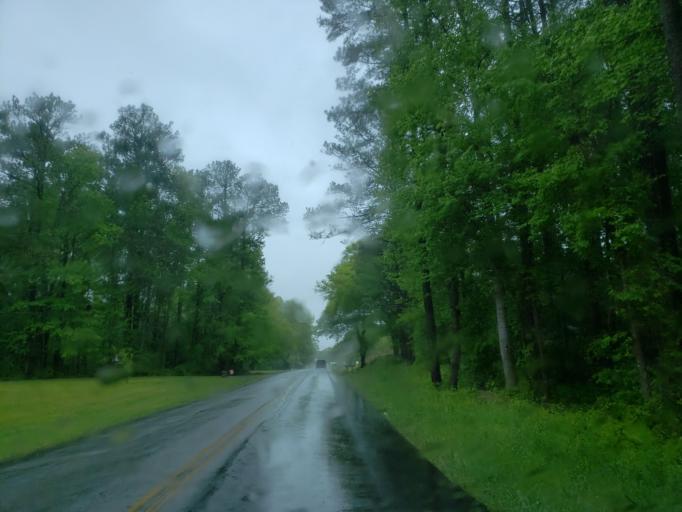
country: US
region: Georgia
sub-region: Haralson County
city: Bremen
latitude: 33.6949
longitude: -85.1876
